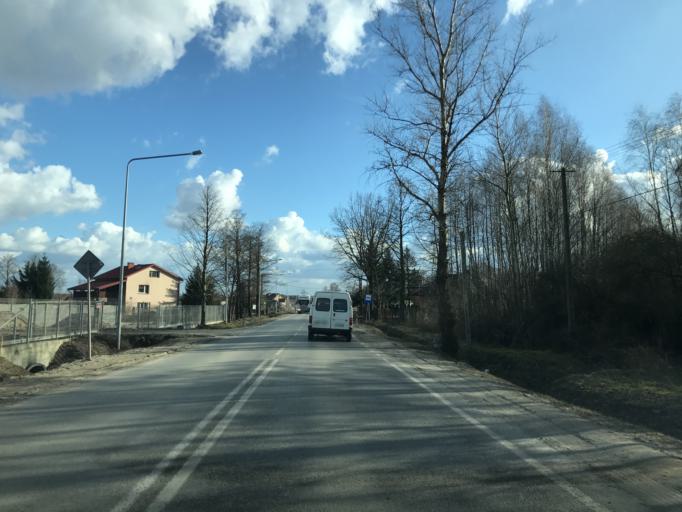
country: PL
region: Masovian Voivodeship
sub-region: Powiat wolominski
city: Radzymin
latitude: 52.4004
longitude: 21.1952
